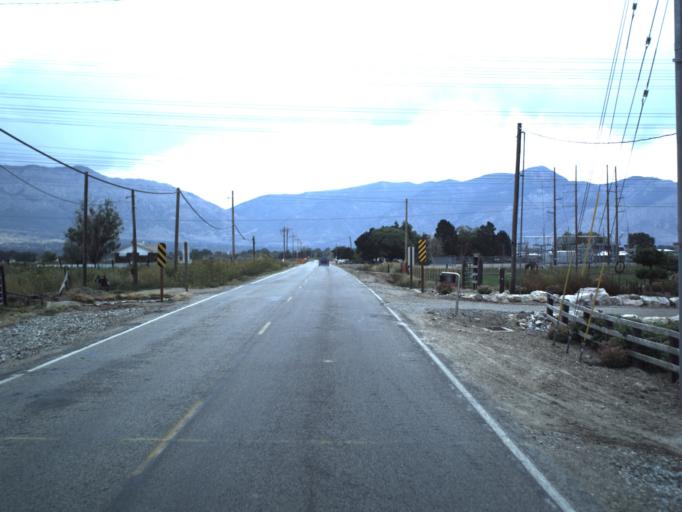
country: US
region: Utah
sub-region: Weber County
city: Plain City
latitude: 41.3050
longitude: -112.0582
